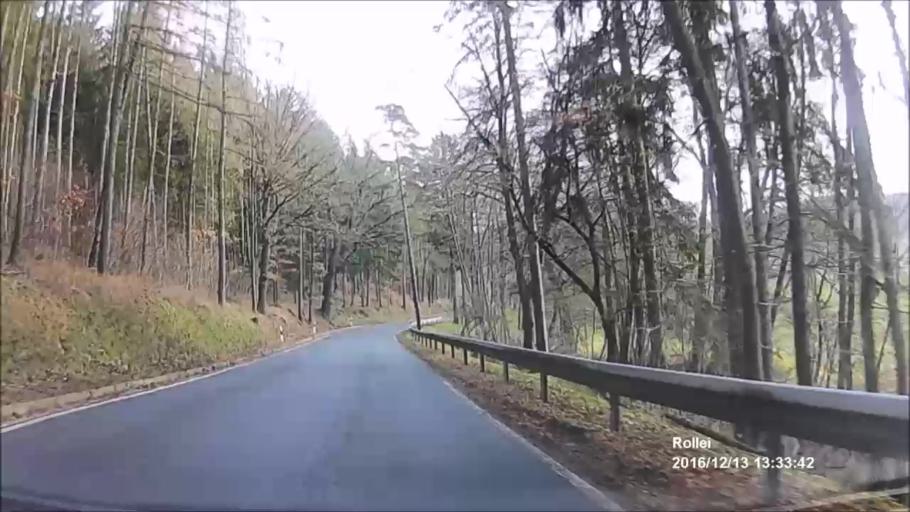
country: DE
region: Thuringia
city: Schwarza
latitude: 50.8506
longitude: 11.2809
